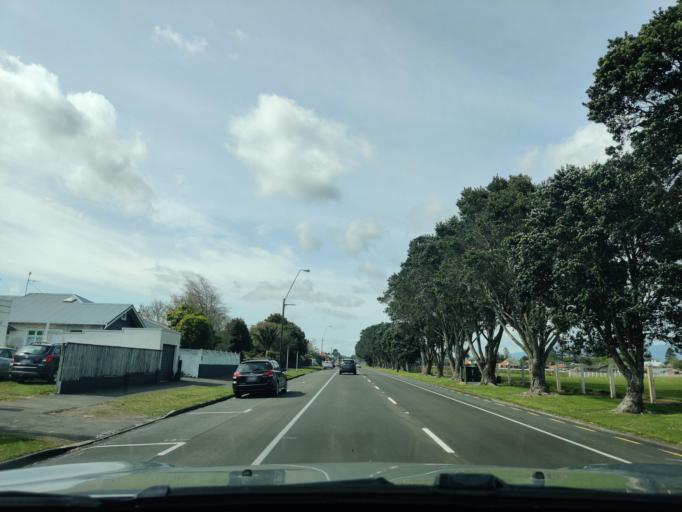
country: NZ
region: Taranaki
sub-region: New Plymouth District
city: New Plymouth
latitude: -39.0662
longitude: 174.0882
